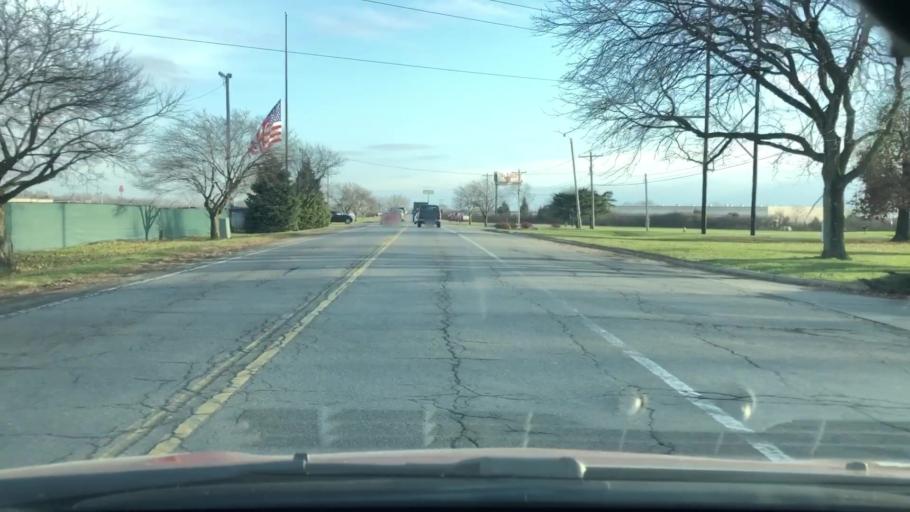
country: US
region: Ohio
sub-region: Franklin County
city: Obetz
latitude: 39.8737
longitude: -82.9441
